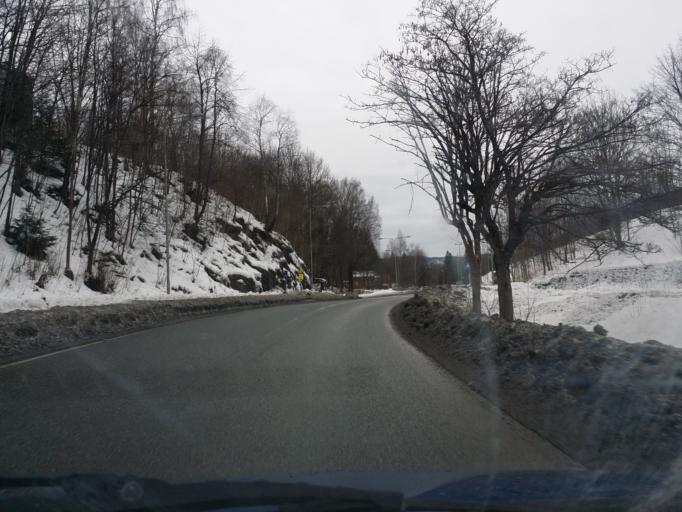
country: NO
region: Akershus
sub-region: Asker
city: Billingstad
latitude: 59.8992
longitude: 10.4955
